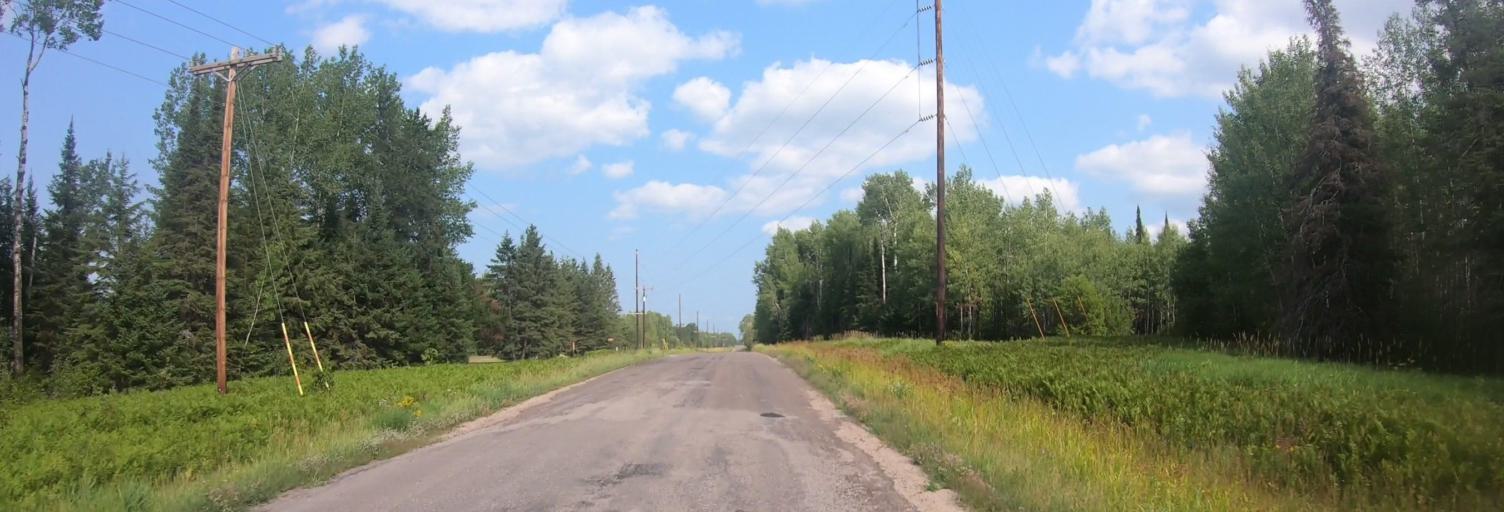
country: US
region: Minnesota
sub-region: Saint Louis County
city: Mountain Iron
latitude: 47.8921
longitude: -92.7306
